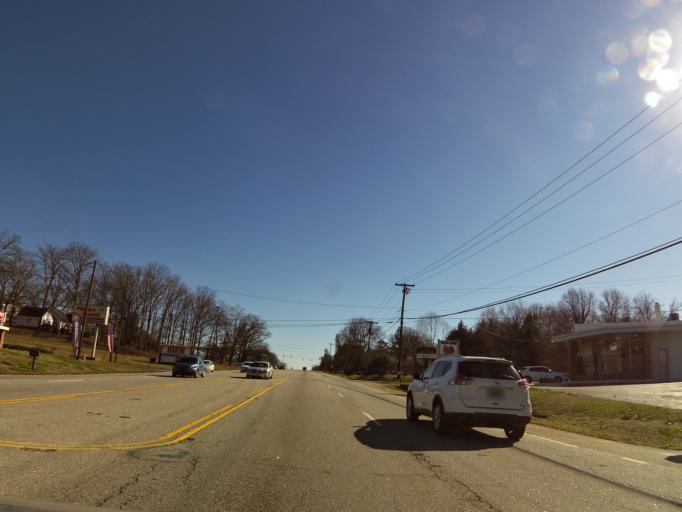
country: US
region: South Carolina
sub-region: Greenville County
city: Sans Souci
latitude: 34.9001
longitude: -82.4152
